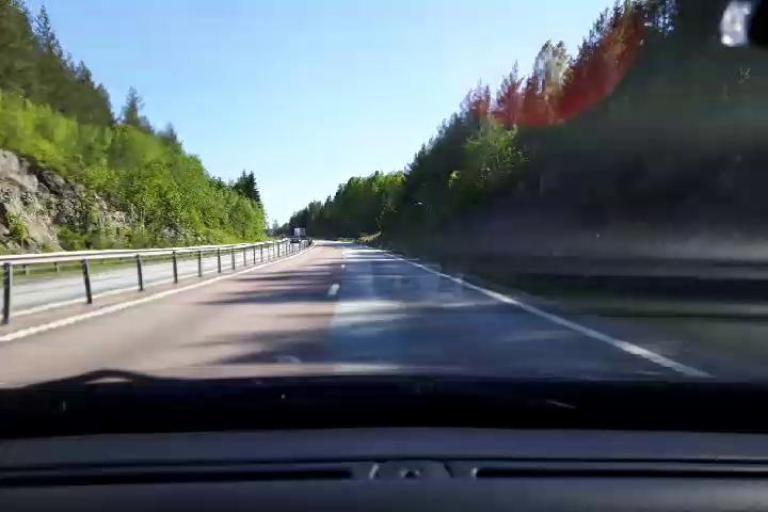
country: SE
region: Gaevleborg
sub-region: Soderhamns Kommun
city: Soderhamn
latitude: 61.2720
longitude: 17.0264
